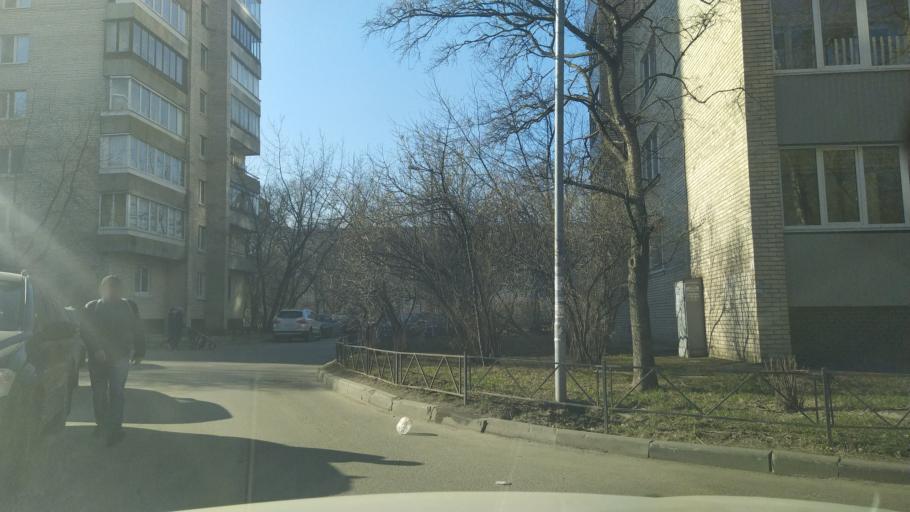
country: RU
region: Leningrad
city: Akademicheskoe
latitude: 60.0189
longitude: 30.3907
